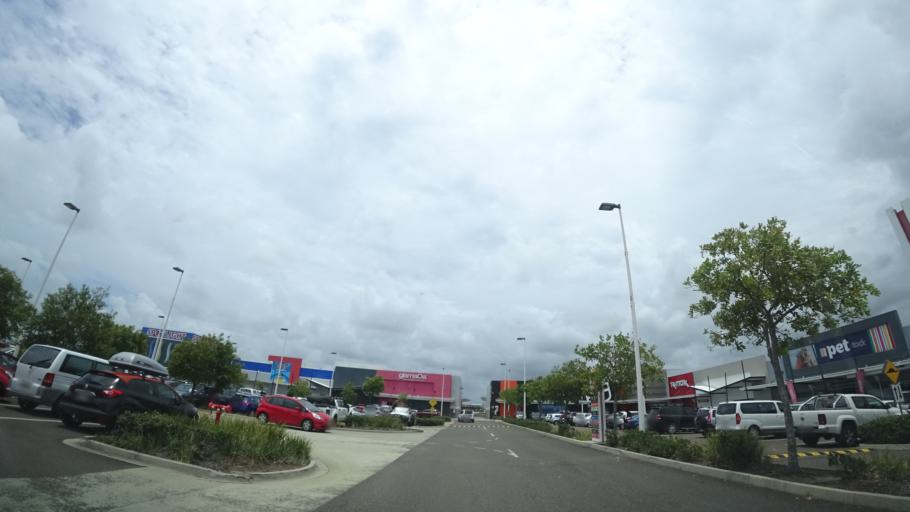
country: AU
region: Queensland
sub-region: Sunshine Coast
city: Dicky Beach
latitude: -26.7369
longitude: 153.1192
